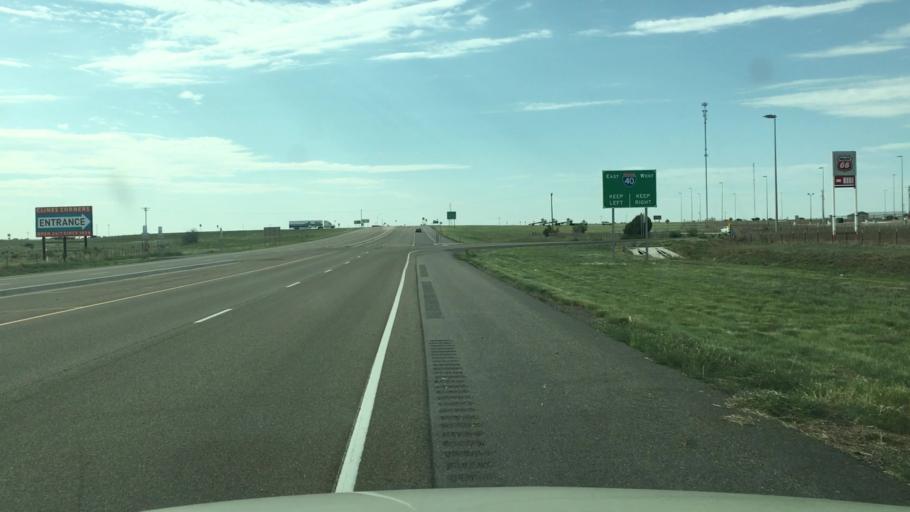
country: US
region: New Mexico
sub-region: Torrance County
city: Moriarty
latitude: 35.0130
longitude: -105.6669
